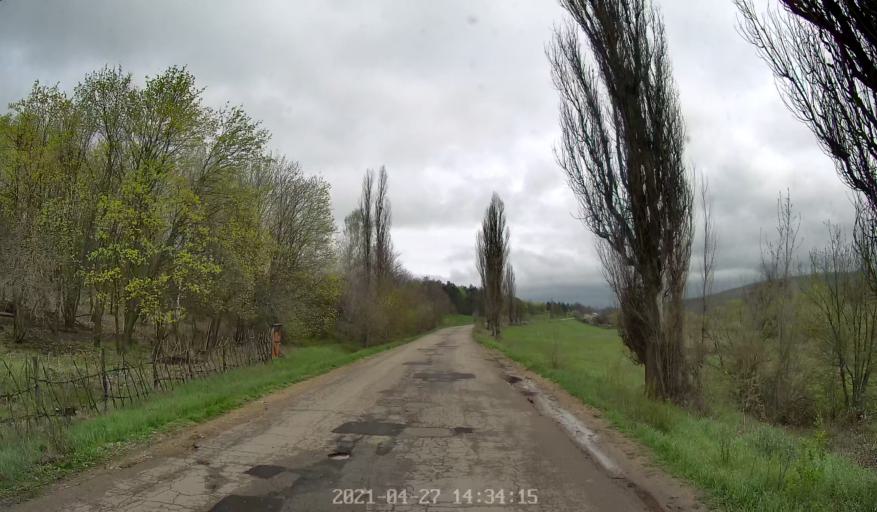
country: MD
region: Chisinau
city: Vadul lui Voda
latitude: 47.0575
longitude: 29.0282
